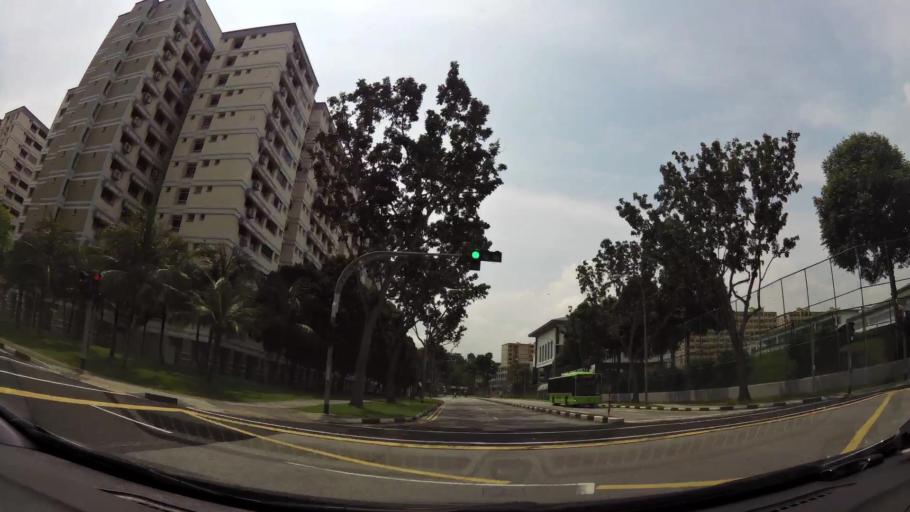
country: MY
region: Johor
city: Kampung Pasir Gudang Baru
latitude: 1.3733
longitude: 103.9609
